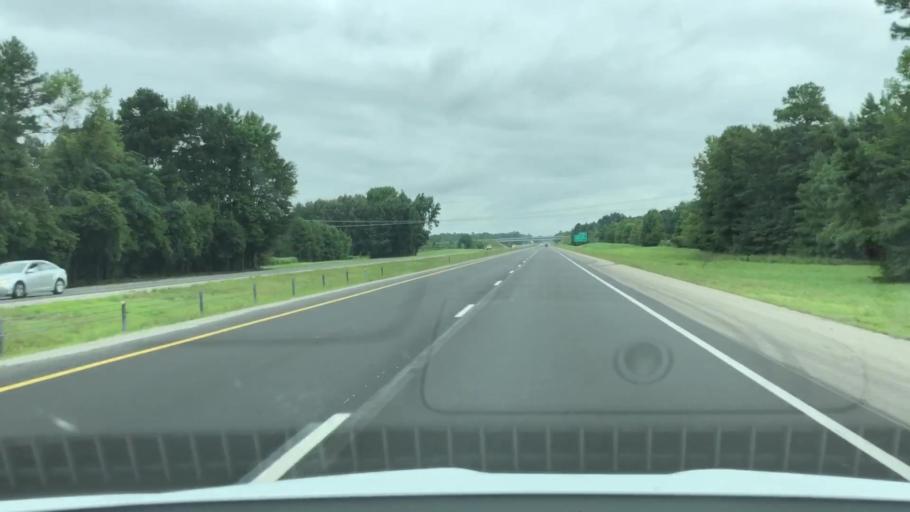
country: US
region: North Carolina
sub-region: Wayne County
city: Fremont
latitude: 35.5987
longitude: -77.9809
